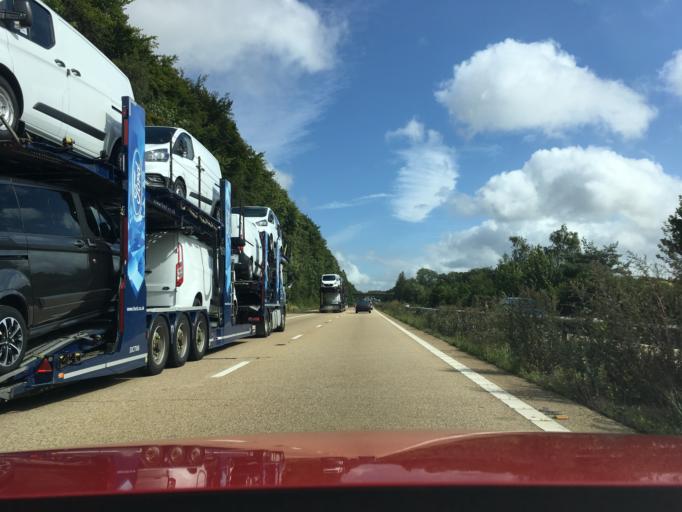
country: GB
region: England
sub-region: Hampshire
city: Overton
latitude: 51.1738
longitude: -1.2229
